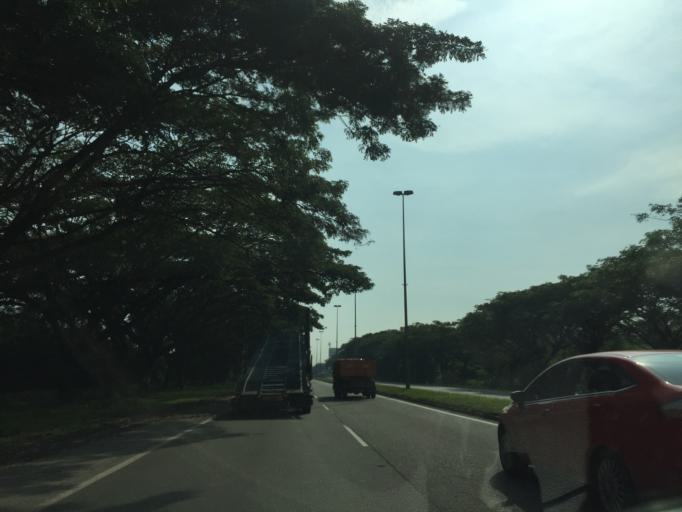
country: MY
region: Selangor
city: Klang
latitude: 2.9837
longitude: 101.4357
